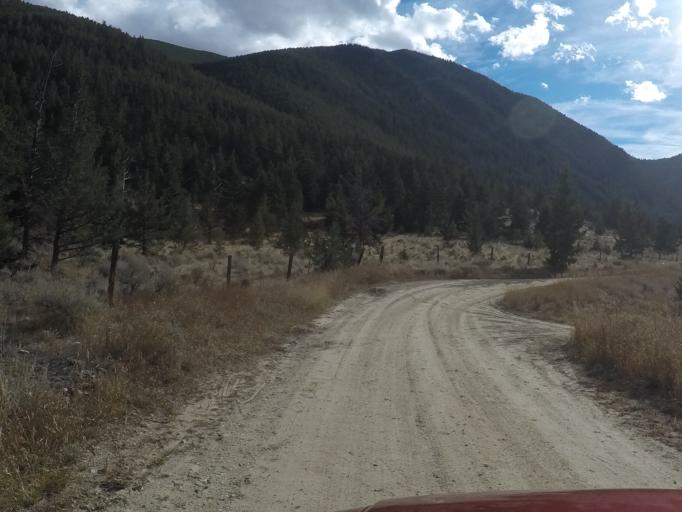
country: US
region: Montana
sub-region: Carbon County
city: Red Lodge
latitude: 45.0937
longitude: -109.3141
